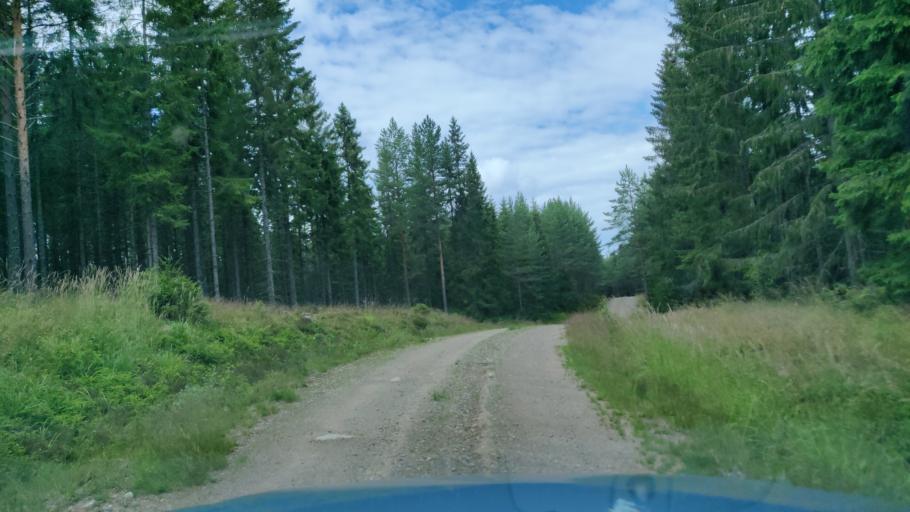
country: SE
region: Vaermland
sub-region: Hagfors Kommun
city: Hagfors
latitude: 59.9583
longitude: 13.5895
